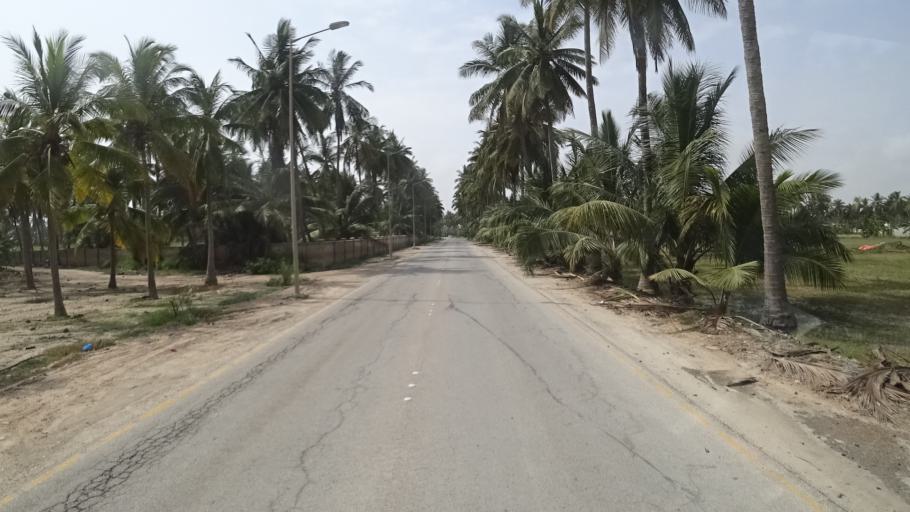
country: OM
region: Zufar
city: Salalah
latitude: 17.0119
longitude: 54.1531
